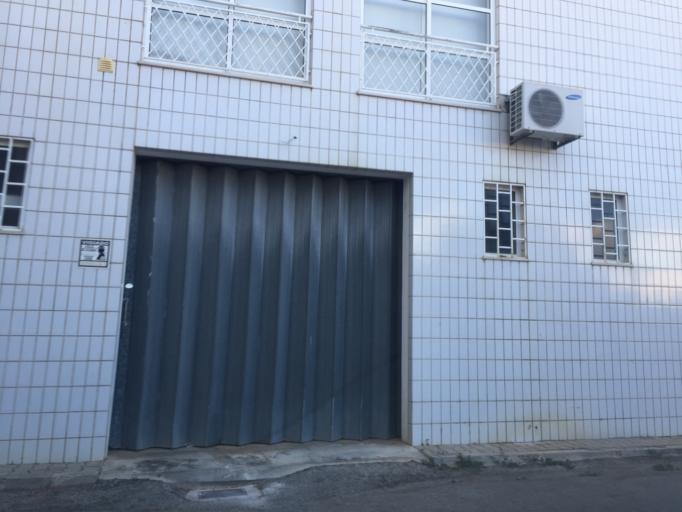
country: PT
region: Faro
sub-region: Tavira
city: Tavira
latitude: 37.1328
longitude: -7.6445
